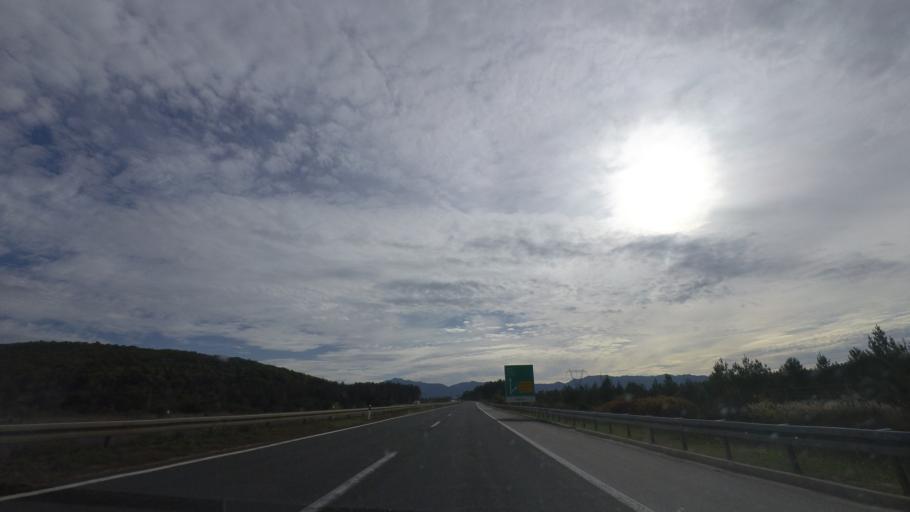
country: HR
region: Licko-Senjska
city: Gospic
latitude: 44.5878
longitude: 15.4334
